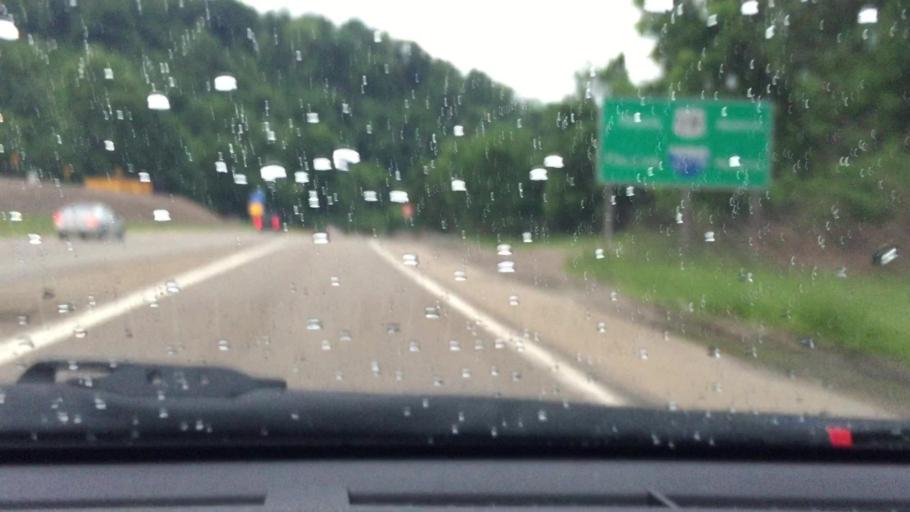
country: US
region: Pennsylvania
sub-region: Allegheny County
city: Green Tree
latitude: 40.4263
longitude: -80.0299
